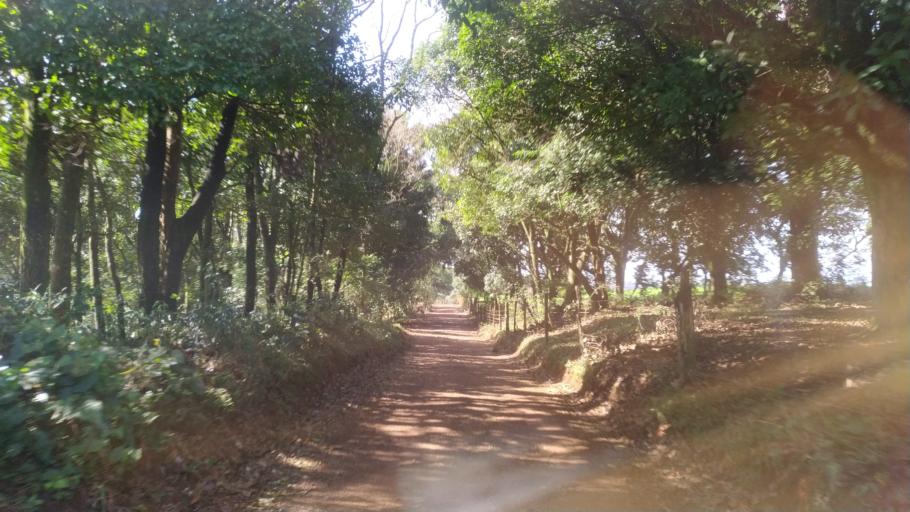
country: BR
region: Santa Catarina
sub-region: Chapeco
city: Chapeco
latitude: -27.1621
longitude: -52.6011
